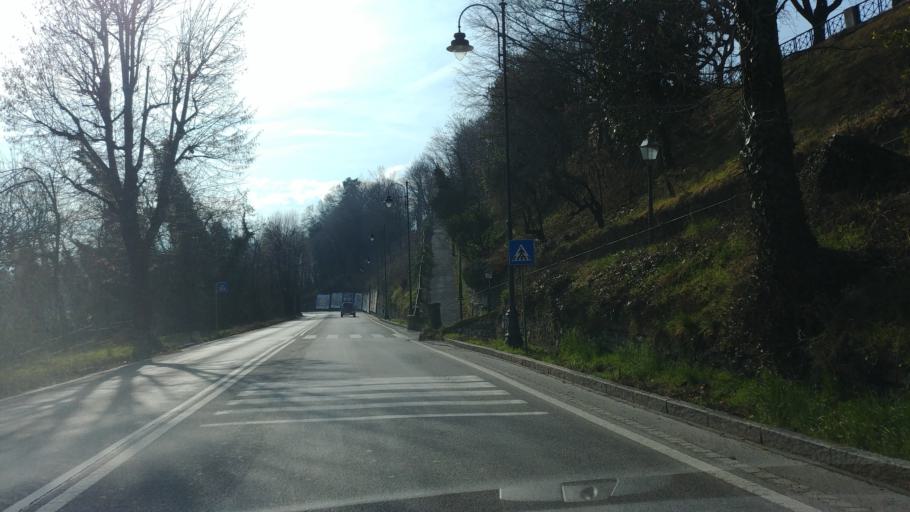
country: IT
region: Piedmont
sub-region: Provincia di Cuneo
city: Cuneo
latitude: 44.3945
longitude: 7.5547
